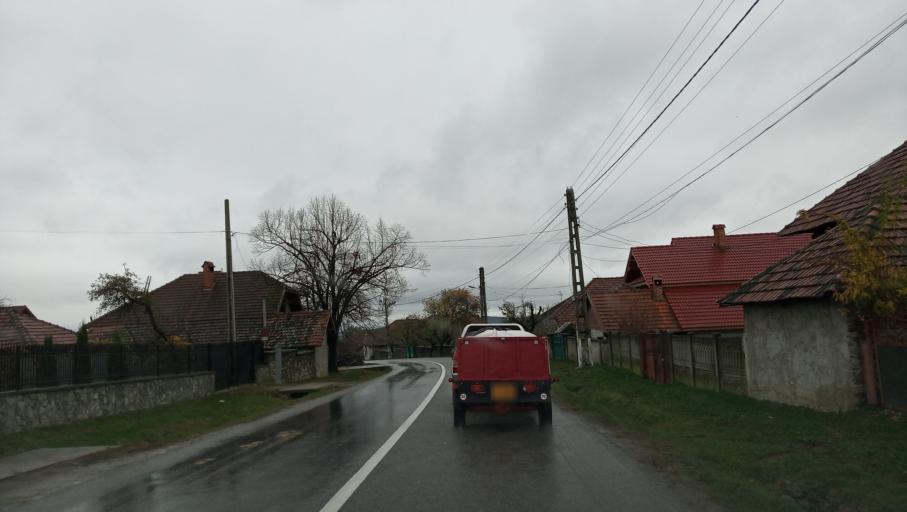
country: RO
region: Gorj
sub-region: Comuna Crasna
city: Carpinis
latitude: 45.1844
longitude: 23.5494
